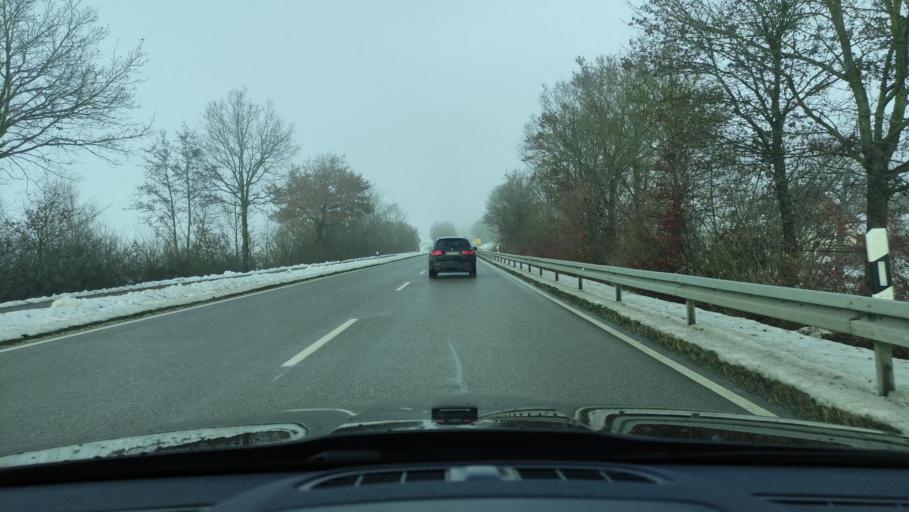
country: DE
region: Bavaria
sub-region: Swabia
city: Deisenhausen
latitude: 48.2723
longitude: 10.3414
